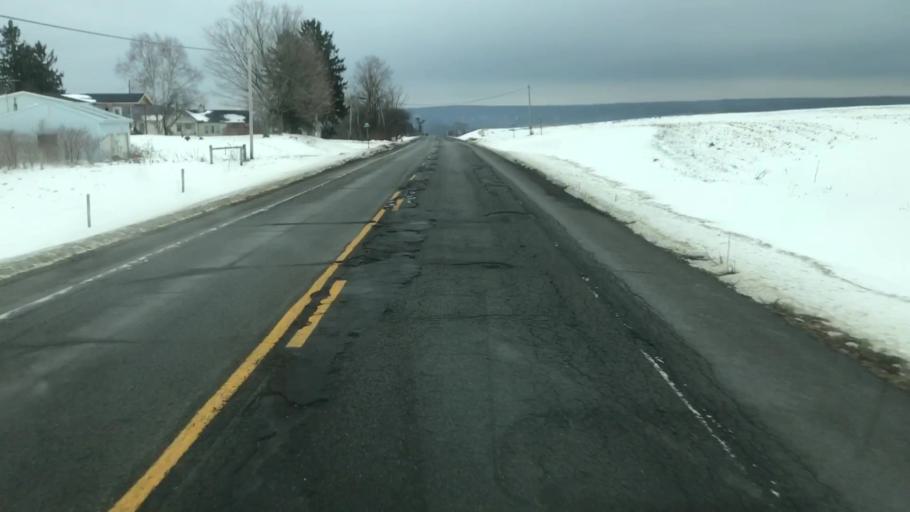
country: US
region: New York
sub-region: Cayuga County
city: Moravia
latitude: 42.7161
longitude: -76.3128
